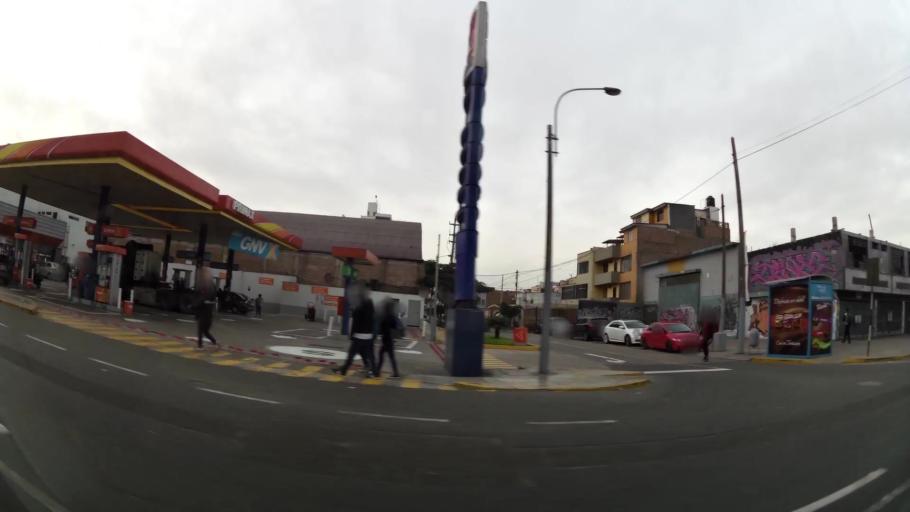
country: PE
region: Callao
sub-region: Callao
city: Callao
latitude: -12.0755
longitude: -77.0970
